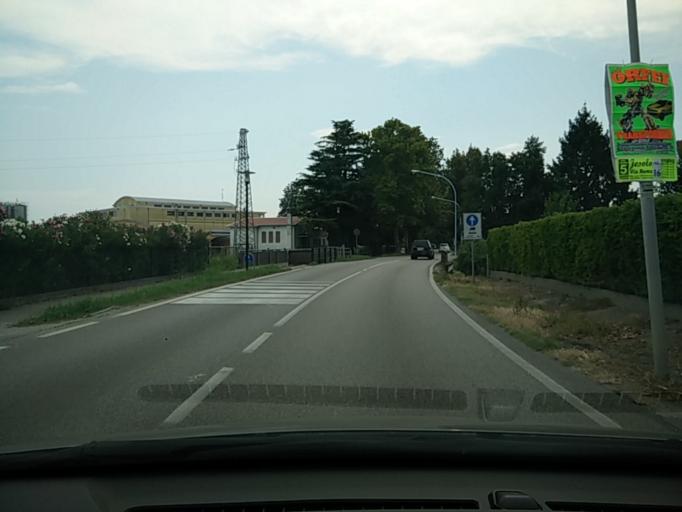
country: IT
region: Veneto
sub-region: Provincia di Venezia
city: Iesolo
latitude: 45.5414
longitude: 12.6493
